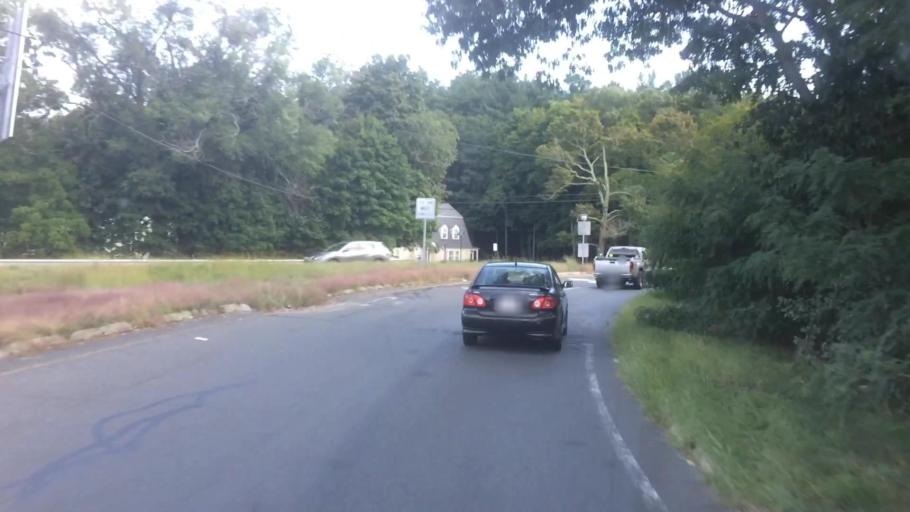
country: US
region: Massachusetts
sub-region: Middlesex County
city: Woburn
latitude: 42.4983
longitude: -71.1579
